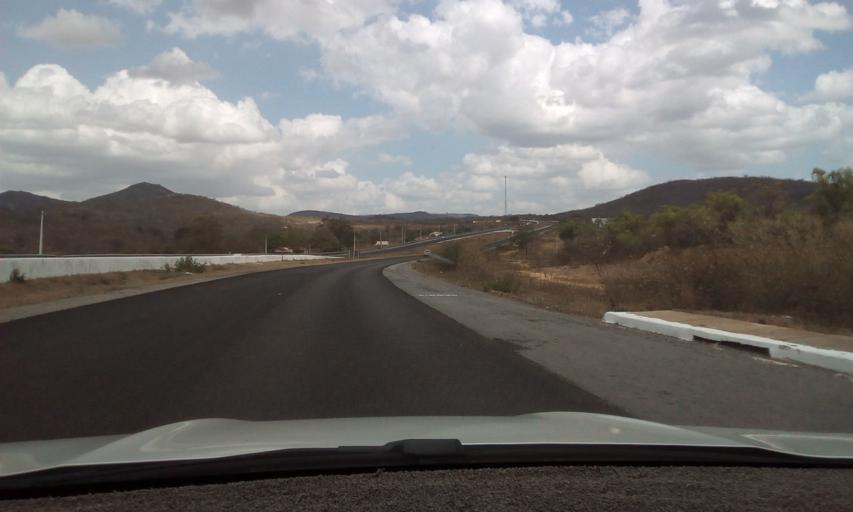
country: BR
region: Pernambuco
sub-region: Toritama
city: Toritama
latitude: -8.1154
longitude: -36.0068
